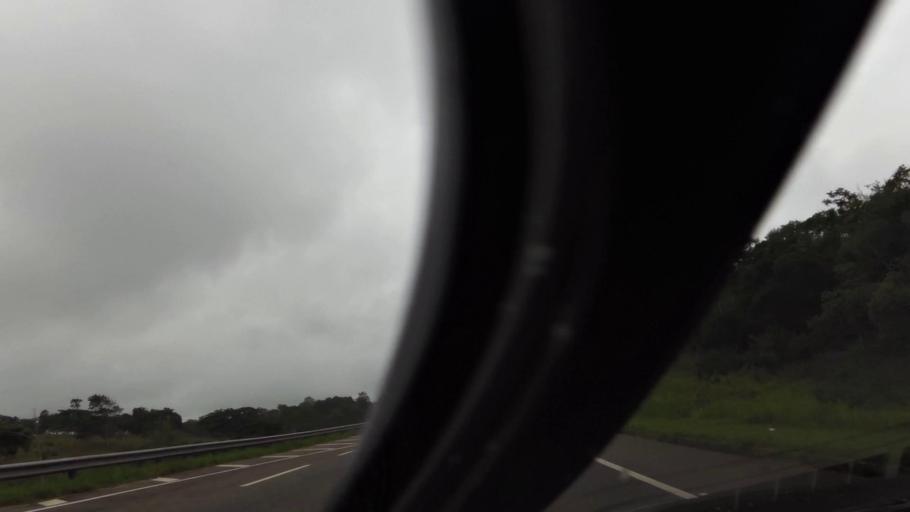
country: BR
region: Espirito Santo
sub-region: Guarapari
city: Guarapari
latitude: -20.7087
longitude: -40.5759
